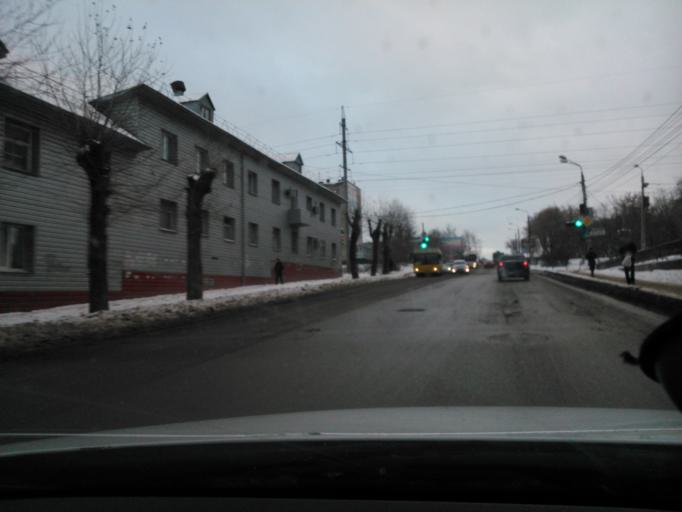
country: RU
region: Perm
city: Kondratovo
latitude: 57.9709
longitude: 56.1711
